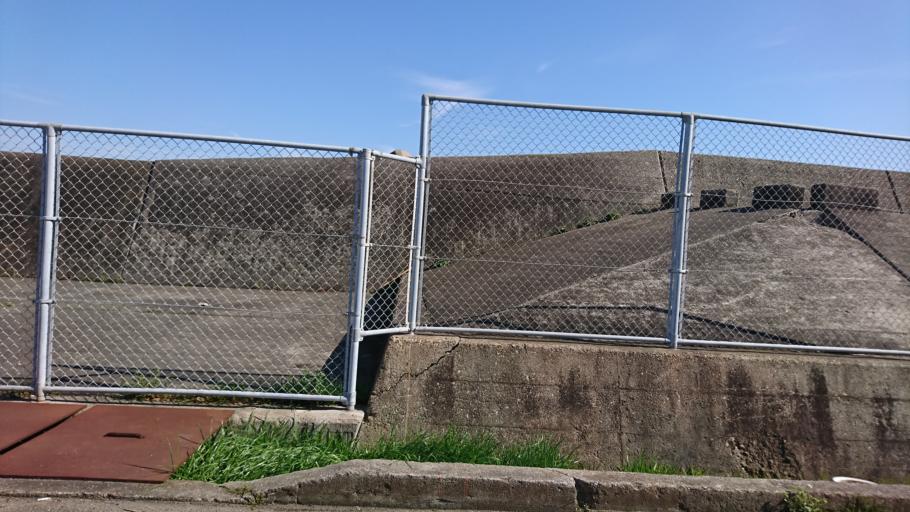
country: JP
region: Hyogo
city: Kakogawacho-honmachi
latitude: 34.6946
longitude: 134.8534
